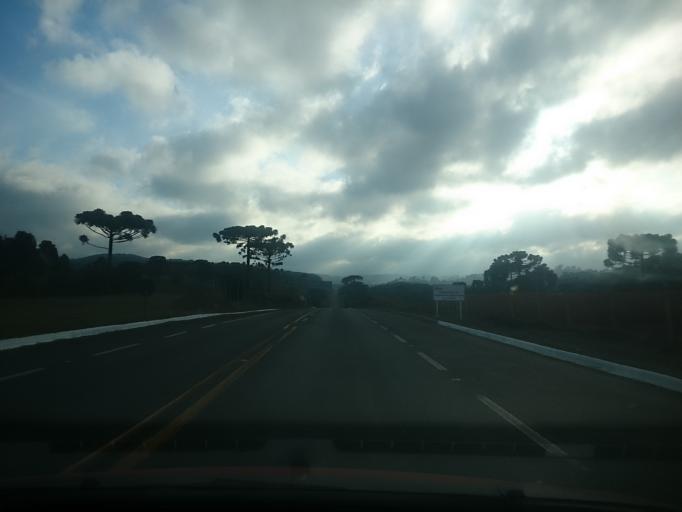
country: BR
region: Santa Catarina
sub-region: Lages
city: Lages
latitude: -28.0050
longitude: -50.5395
